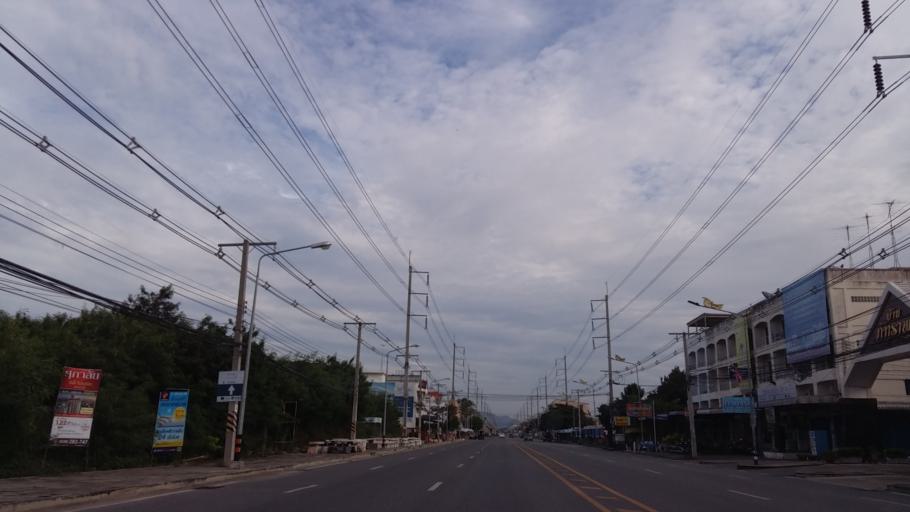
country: TH
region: Chon Buri
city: Chon Buri
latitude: 13.3307
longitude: 100.9367
